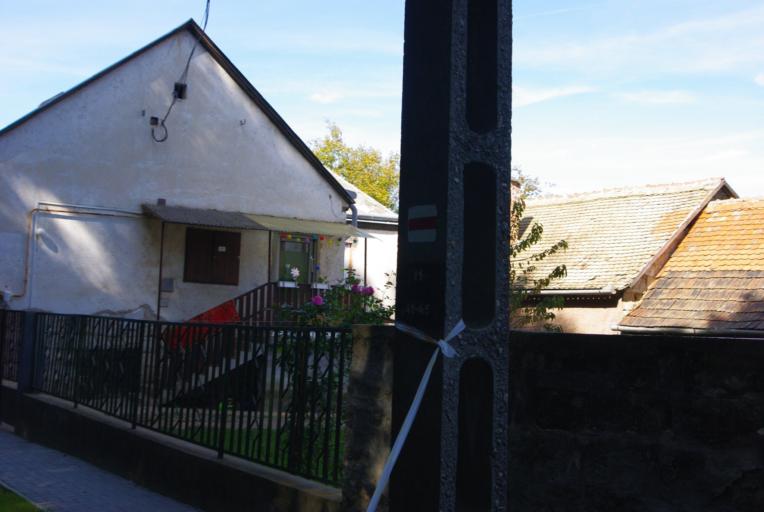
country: HU
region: Pest
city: Toeroekbalint
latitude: 47.4315
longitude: 18.9199
